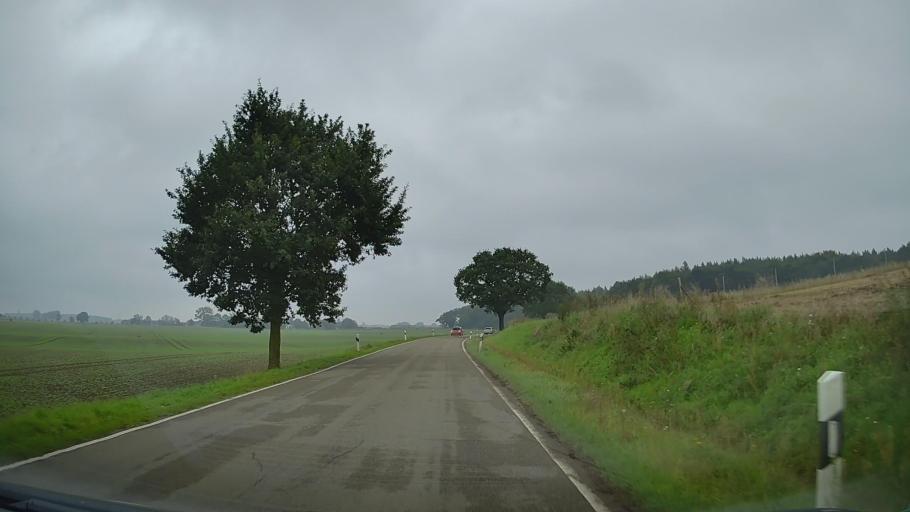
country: DE
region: Mecklenburg-Vorpommern
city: Blowatz
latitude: 53.9668
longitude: 11.5507
